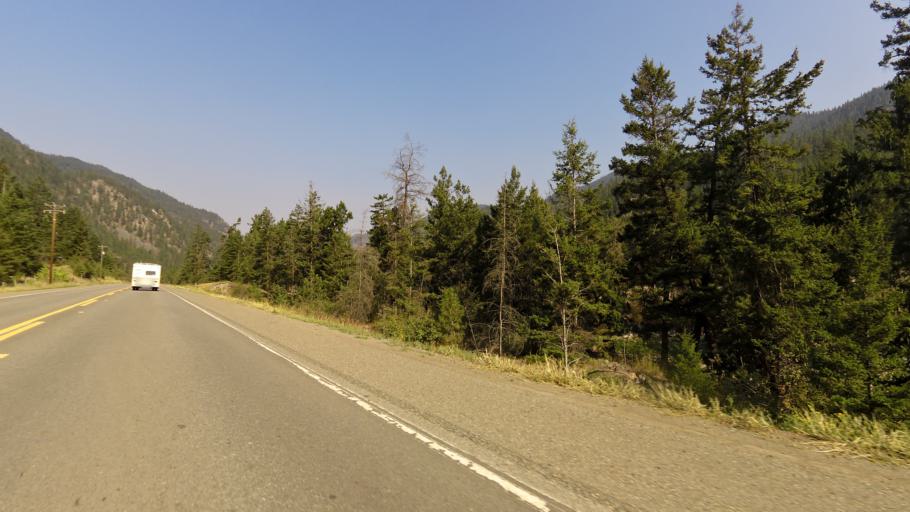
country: CA
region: British Columbia
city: Princeton
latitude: 49.3818
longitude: -120.1885
